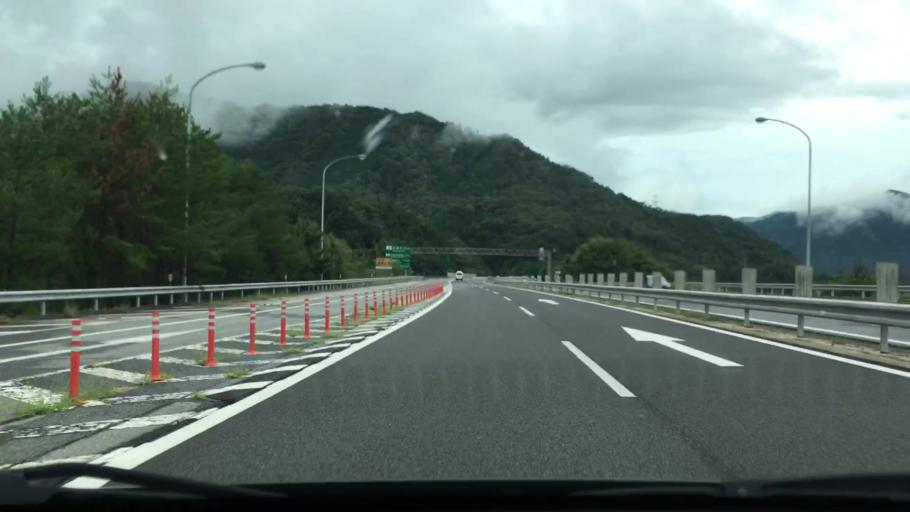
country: JP
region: Hiroshima
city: Hiroshima-shi
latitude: 34.5714
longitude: 132.4563
